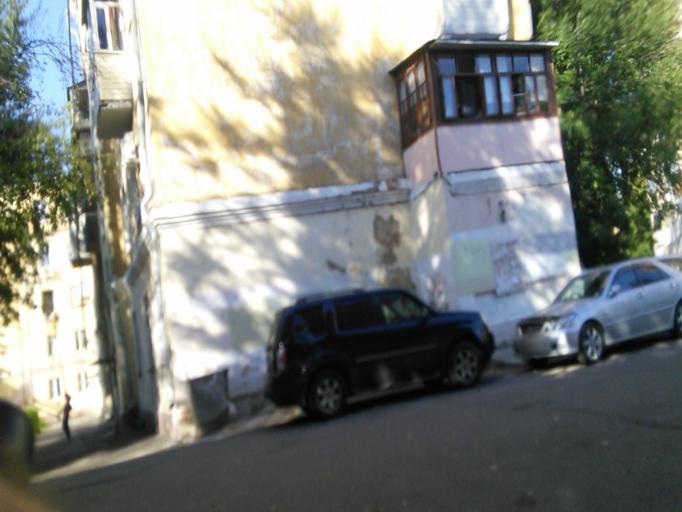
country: RU
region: Moskovskaya
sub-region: Podol'skiy Rayon
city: Podol'sk
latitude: 55.4349
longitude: 37.5637
